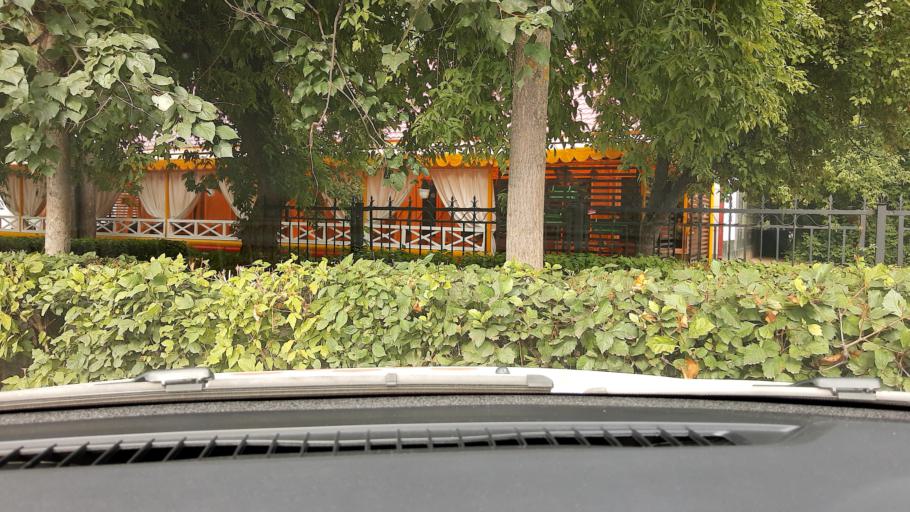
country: RU
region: Nizjnij Novgorod
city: Arzamas
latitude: 55.3983
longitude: 43.8312
